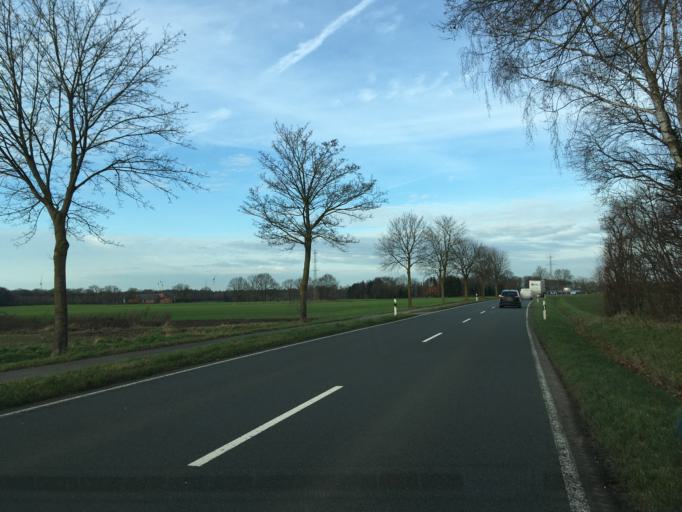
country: DE
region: North Rhine-Westphalia
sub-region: Regierungsbezirk Munster
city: Gescher
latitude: 51.9989
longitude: 7.0366
